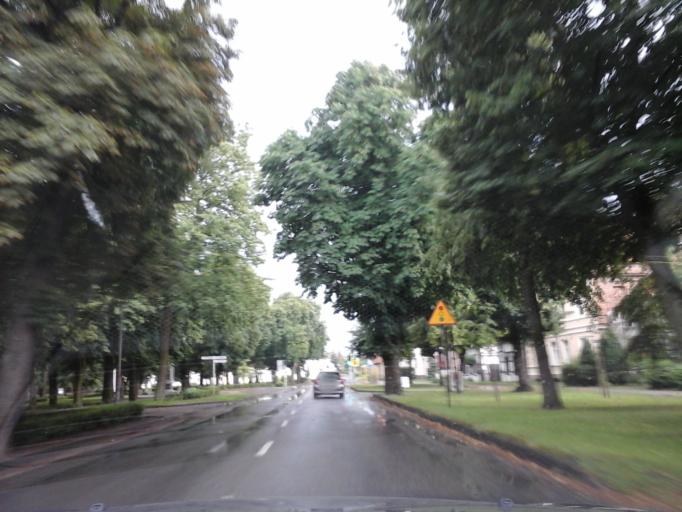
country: PL
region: Greater Poland Voivodeship
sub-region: Powiat miedzychodzki
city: Miedzychod
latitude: 52.5987
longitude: 15.8923
